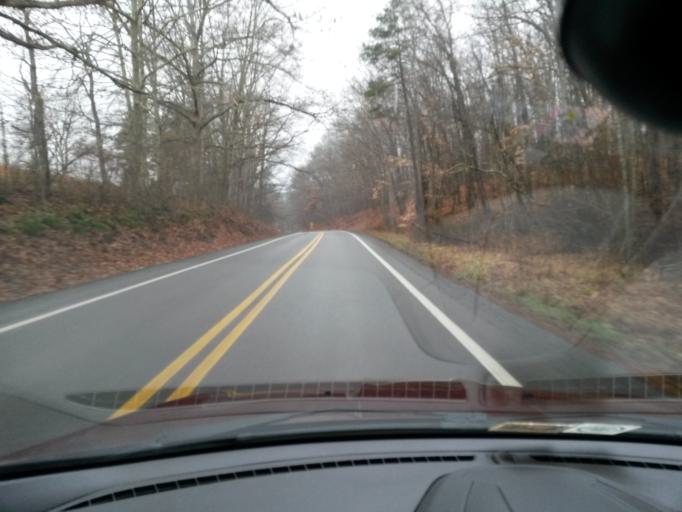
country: US
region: West Virginia
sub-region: Greenbrier County
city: Lewisburg
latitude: 37.8695
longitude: -80.5461
